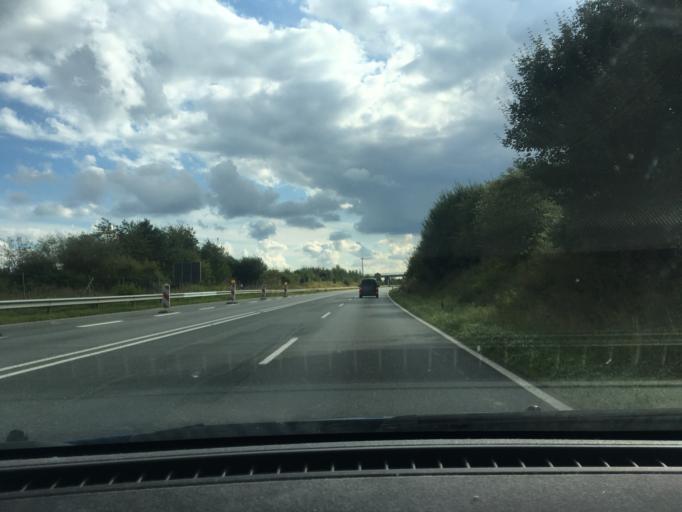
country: DE
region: Lower Saxony
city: Uelzen
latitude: 52.9582
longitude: 10.5896
